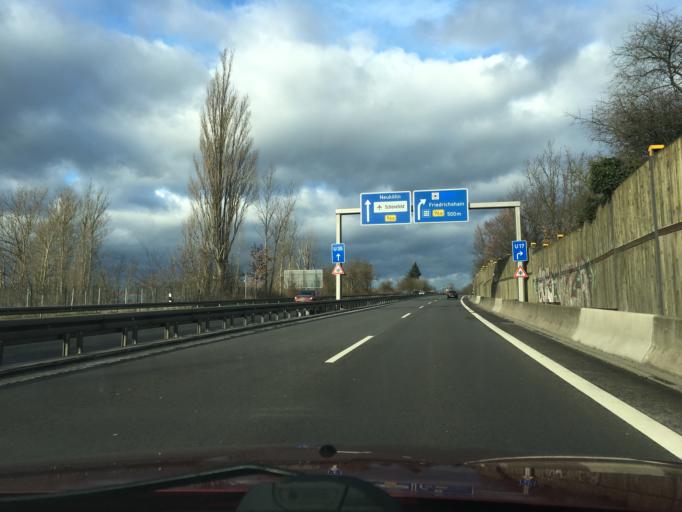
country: DE
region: Berlin
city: Bohnsdorf
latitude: 52.3971
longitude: 13.5602
